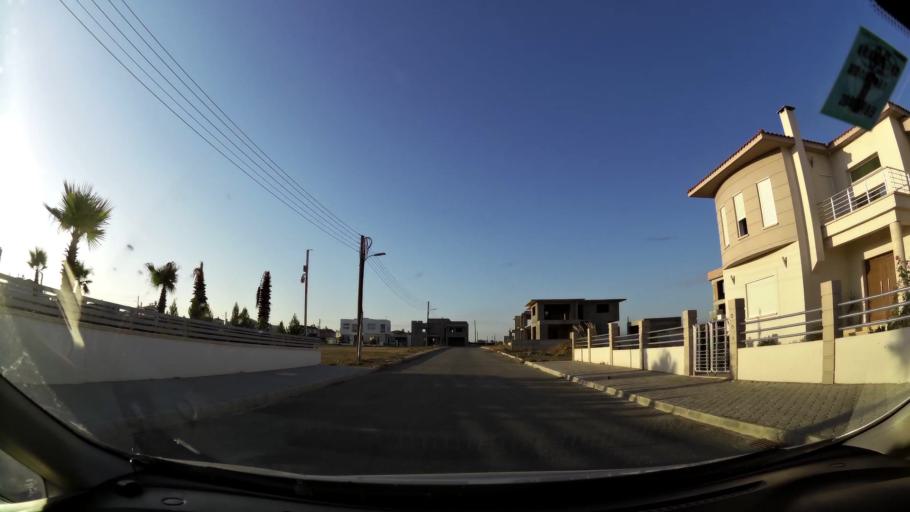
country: CY
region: Lefkosia
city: Nicosia
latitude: 35.1943
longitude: 33.3138
